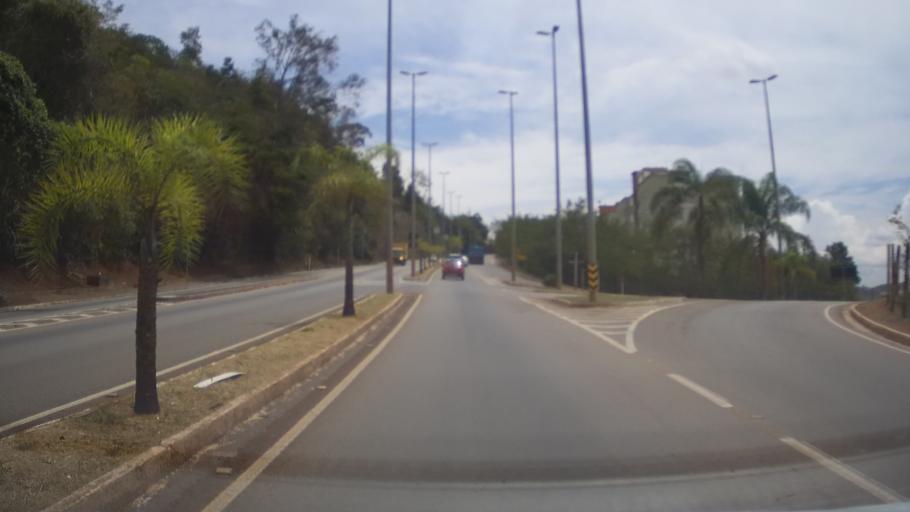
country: BR
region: Minas Gerais
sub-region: Nova Lima
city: Nova Lima
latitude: -19.9962
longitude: -43.8584
